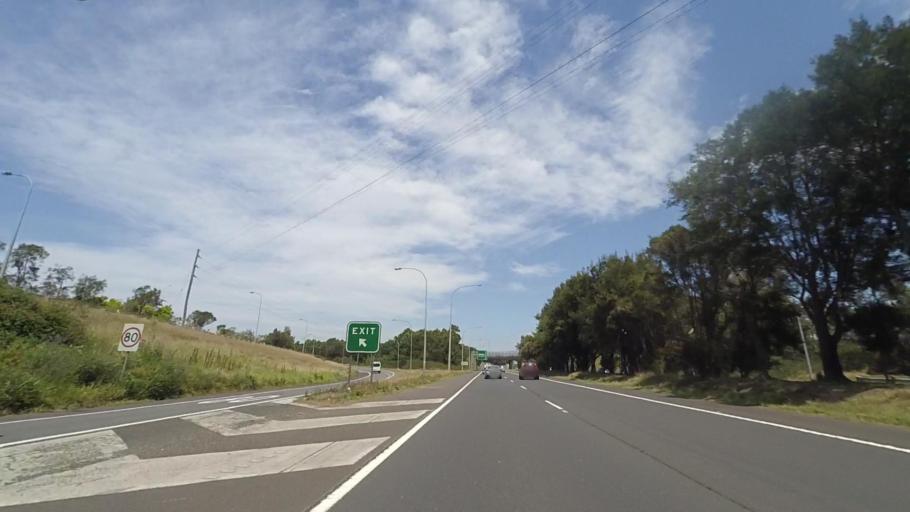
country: AU
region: New South Wales
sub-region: Wollongong
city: Mangerton
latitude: -34.4394
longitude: 150.8660
